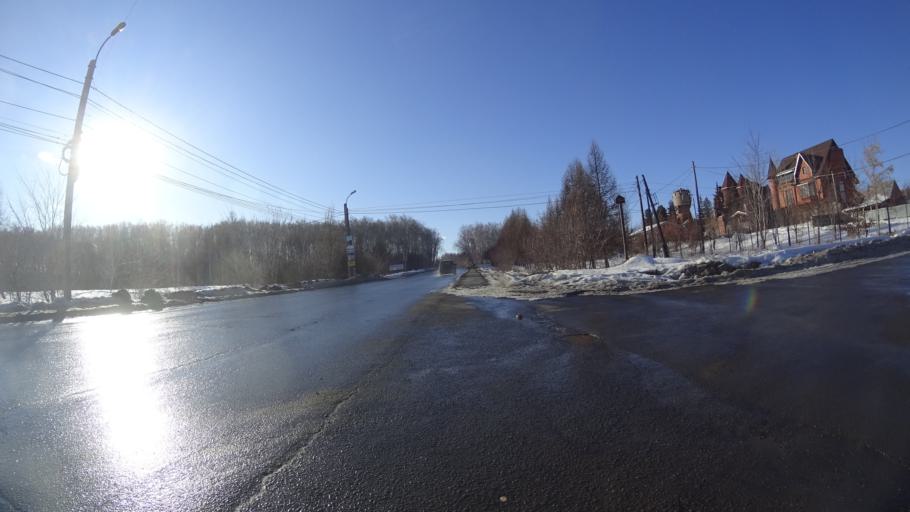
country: RU
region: Chelyabinsk
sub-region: Gorod Chelyabinsk
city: Chelyabinsk
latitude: 55.1488
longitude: 61.2979
